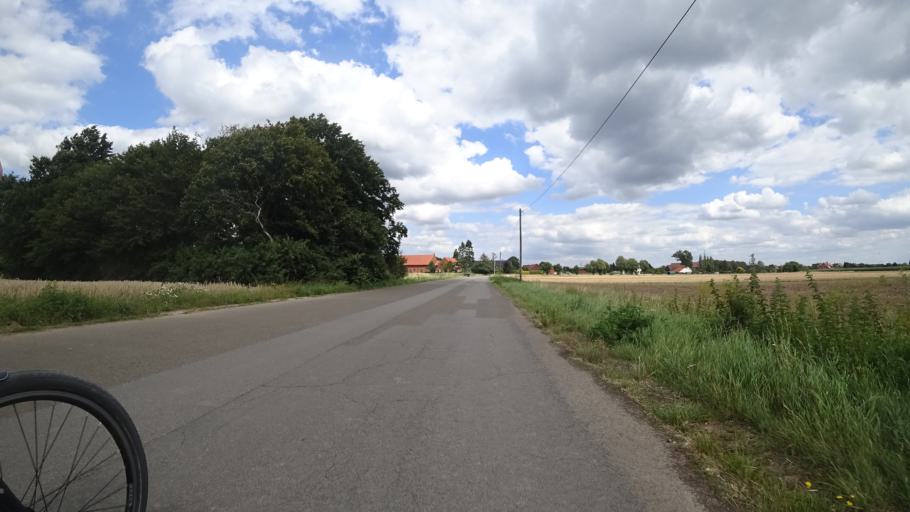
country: DE
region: North Rhine-Westphalia
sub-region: Regierungsbezirk Detmold
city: Petershagen
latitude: 52.4102
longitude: 9.0017
